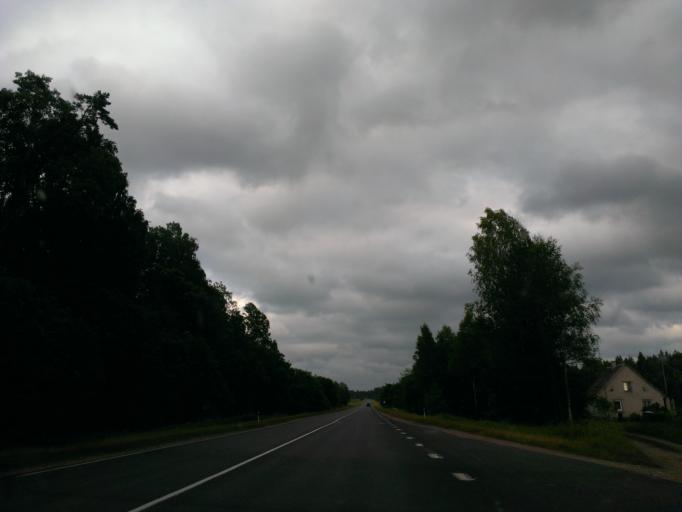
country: LV
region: Skrunda
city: Skrunda
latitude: 56.6800
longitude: 22.1289
